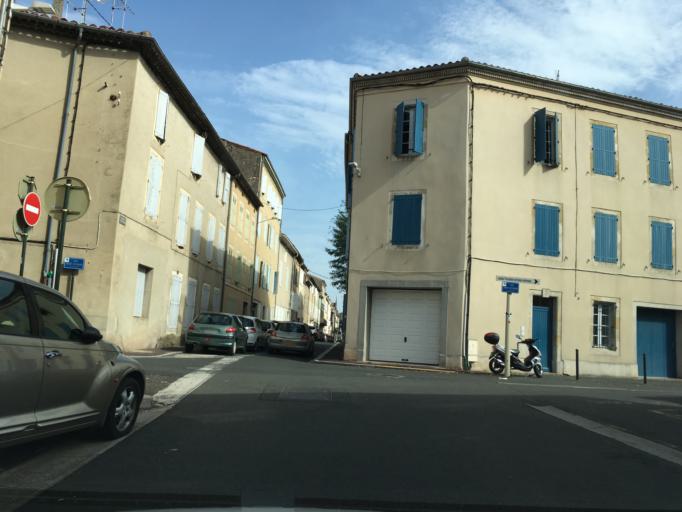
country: FR
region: Midi-Pyrenees
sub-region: Departement du Tarn
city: Castres
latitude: 43.6052
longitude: 2.2461
